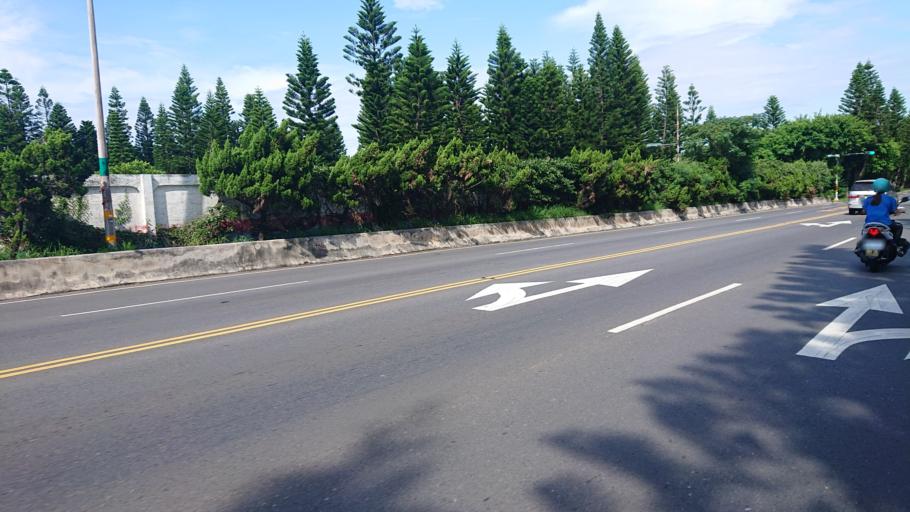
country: TW
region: Taiwan
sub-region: Penghu
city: Ma-kung
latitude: 23.5583
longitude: 119.6009
